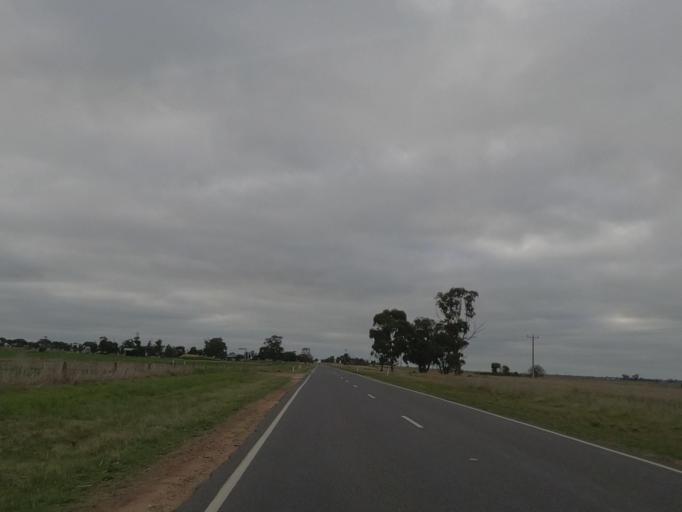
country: AU
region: Victoria
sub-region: Greater Bendigo
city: Long Gully
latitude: -36.5212
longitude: 143.9477
